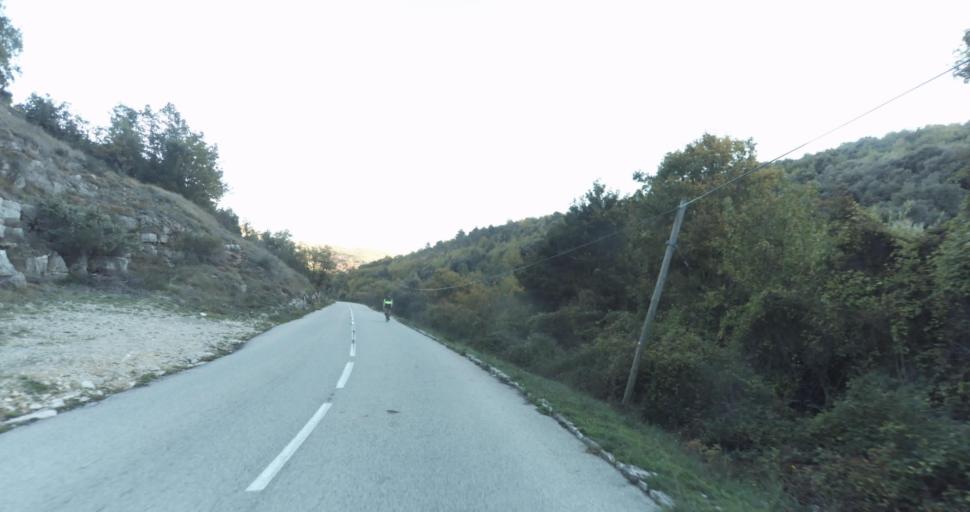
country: FR
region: Provence-Alpes-Cote d'Azur
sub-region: Departement des Alpes-Maritimes
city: Vence
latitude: 43.7487
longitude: 7.0963
